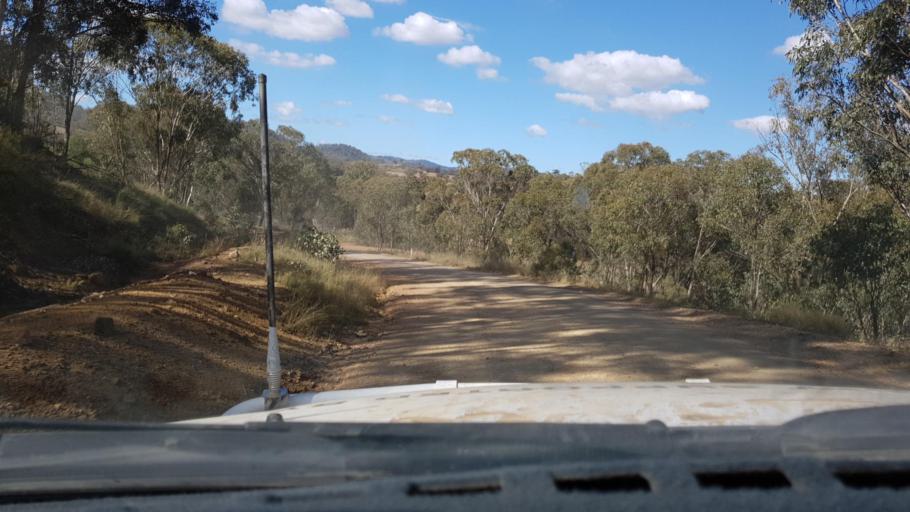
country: AU
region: New South Wales
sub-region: Tamworth Municipality
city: Manilla
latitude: -30.4676
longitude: 150.7440
